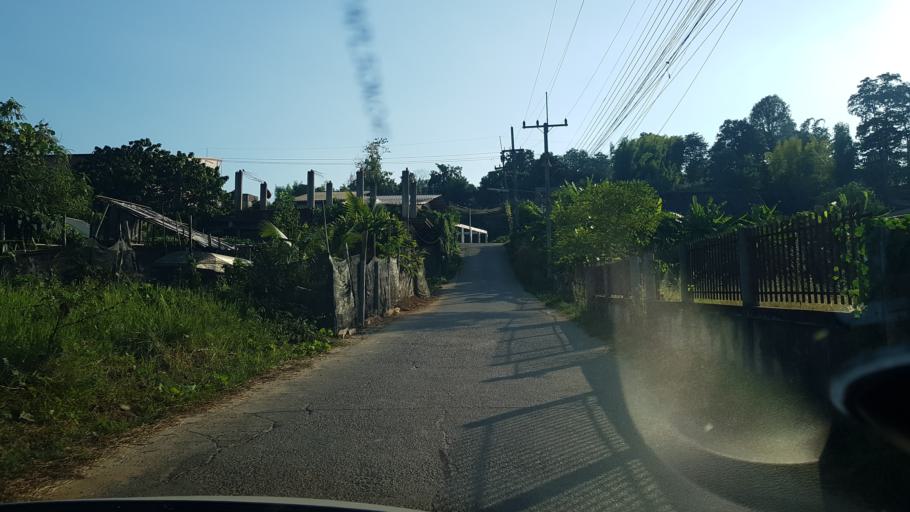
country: TH
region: Chiang Rai
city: Chiang Rai
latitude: 19.9436
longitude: 99.8045
